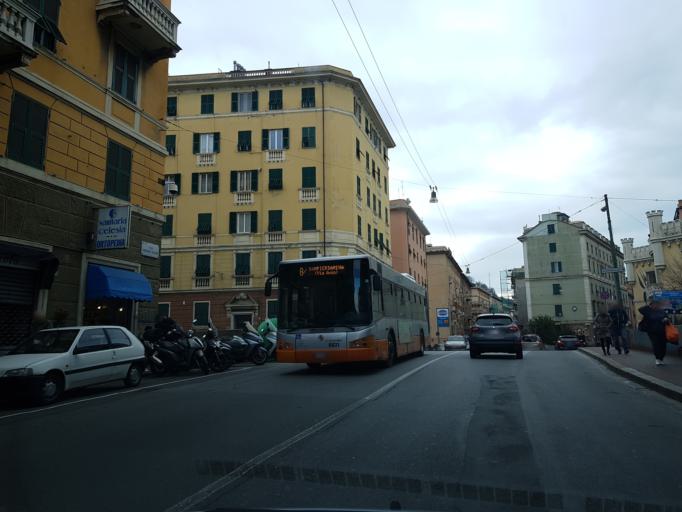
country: IT
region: Liguria
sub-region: Provincia di Genova
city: Genoa
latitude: 44.4350
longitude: 8.8927
